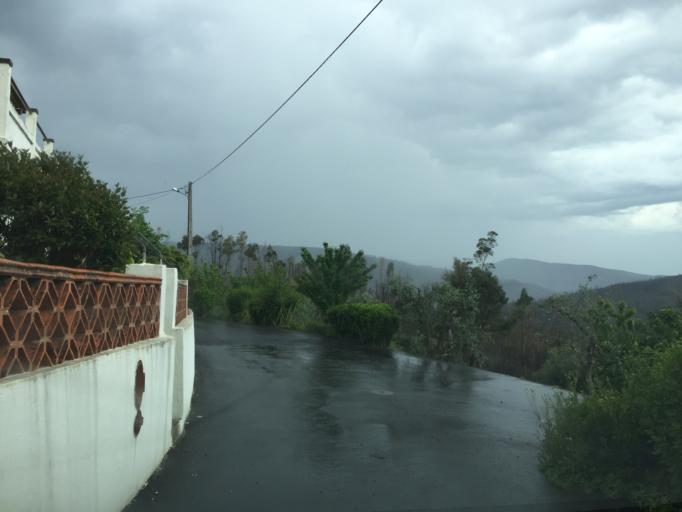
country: PT
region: Coimbra
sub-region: Pampilhosa da Serra
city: Pampilhosa da Serra
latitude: 40.0409
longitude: -8.0026
